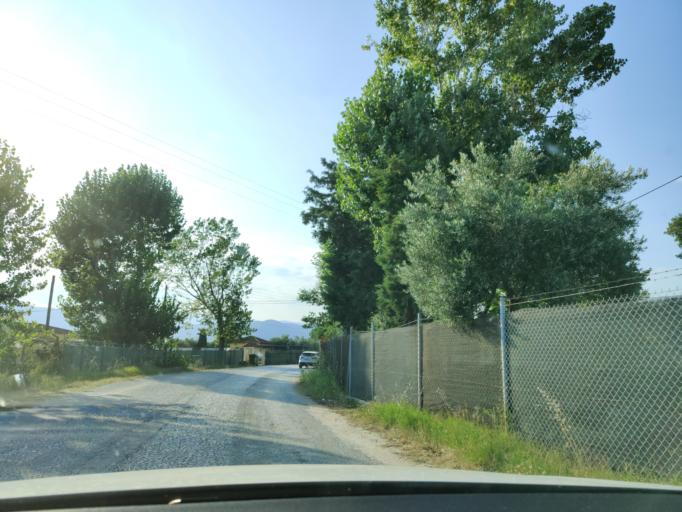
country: GR
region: East Macedonia and Thrace
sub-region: Nomos Kavalas
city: Nea Peramos
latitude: 40.8275
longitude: 24.3059
